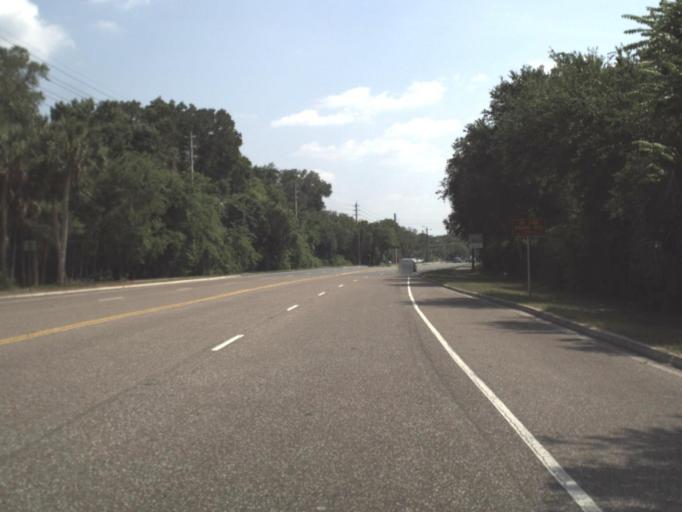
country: US
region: Florida
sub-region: Duval County
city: Atlantic Beach
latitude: 30.3744
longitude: -81.4101
